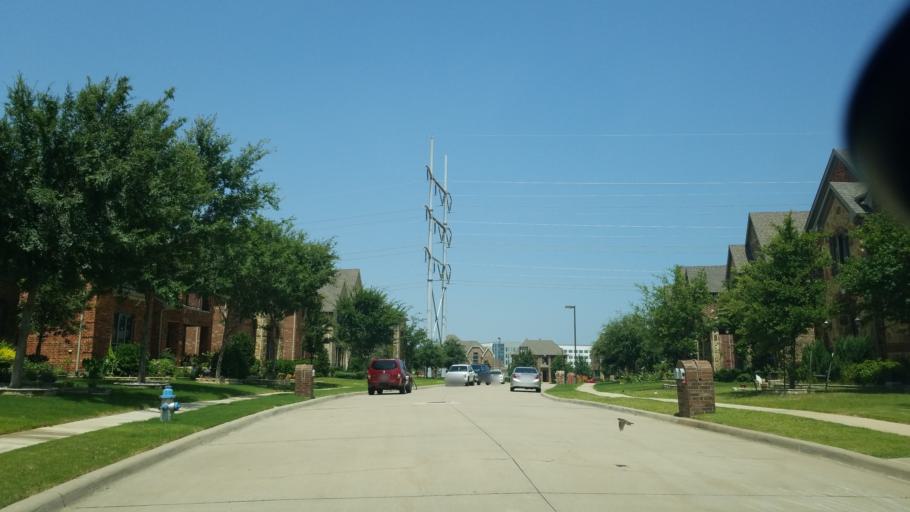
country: US
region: Texas
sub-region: Dallas County
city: Coppell
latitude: 32.9244
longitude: -96.9798
